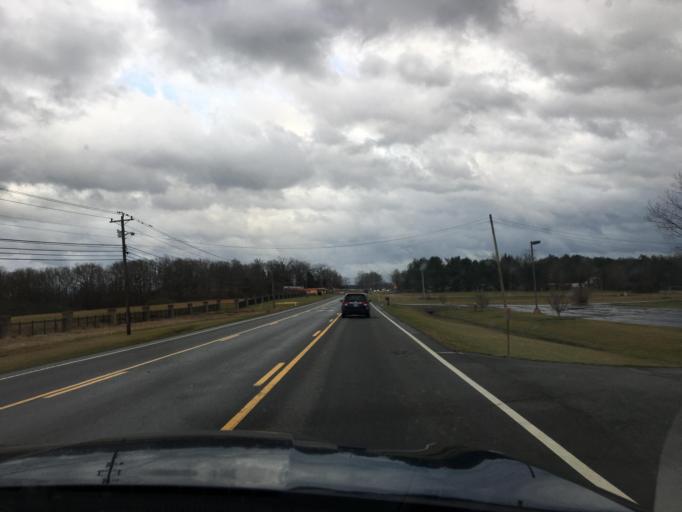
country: US
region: Tennessee
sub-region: Cumberland County
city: Crossville
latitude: 35.9253
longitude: -85.0043
